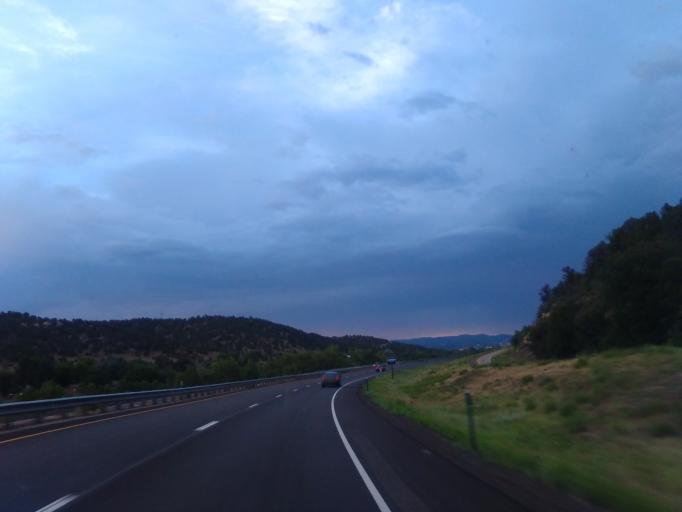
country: US
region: Colorado
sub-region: Las Animas County
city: Trinidad
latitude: 37.1038
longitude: -104.5242
